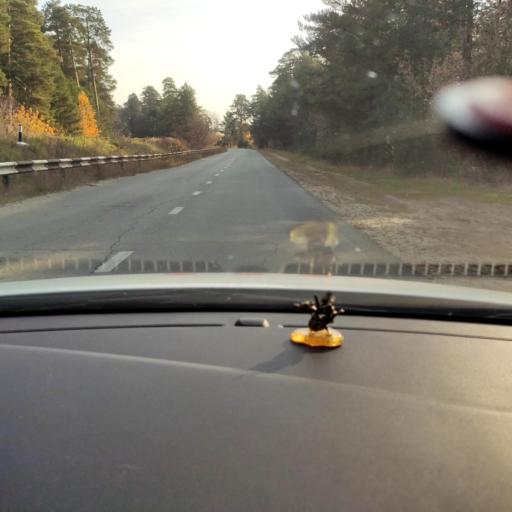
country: RU
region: Tatarstan
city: Osinovo
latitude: 55.8245
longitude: 48.9103
